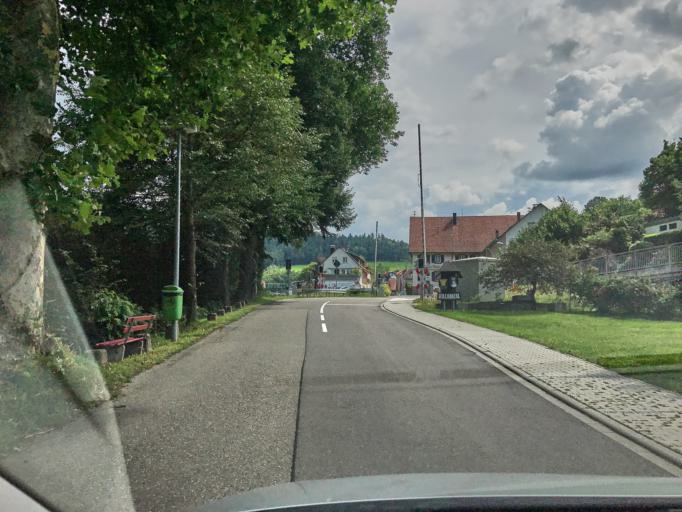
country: DE
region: Baden-Wuerttemberg
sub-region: Freiburg Region
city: Wolfach
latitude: 48.2905
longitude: 8.2673
